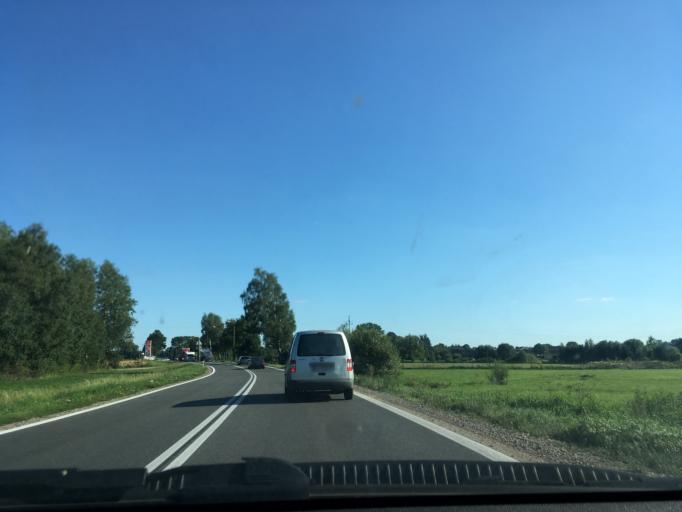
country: PL
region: Podlasie
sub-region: Powiat sokolski
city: Suchowola
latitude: 53.4517
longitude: 23.0875
